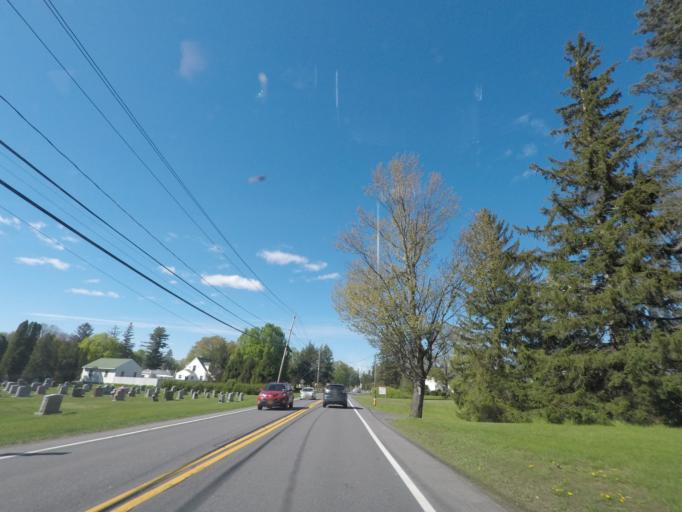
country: US
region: New York
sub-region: Albany County
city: Delmar
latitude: 42.5967
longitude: -73.7953
